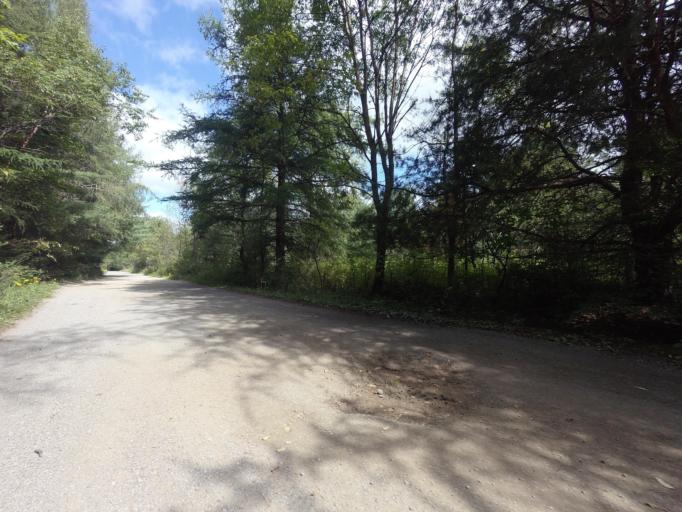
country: CA
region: Ontario
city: Omemee
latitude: 44.7484
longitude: -78.6668
